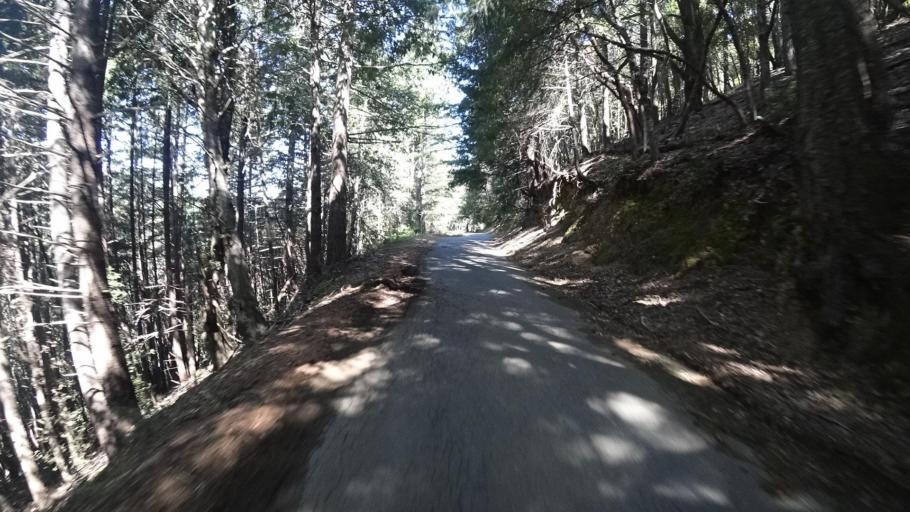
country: US
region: California
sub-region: Humboldt County
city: Redway
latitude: 40.1709
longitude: -124.0875
